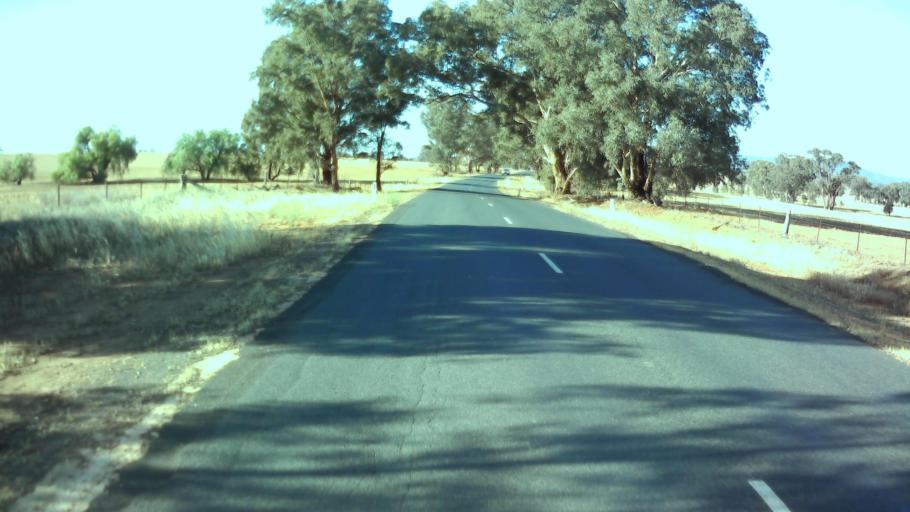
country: AU
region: New South Wales
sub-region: Weddin
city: Grenfell
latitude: -33.9168
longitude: 148.1421
